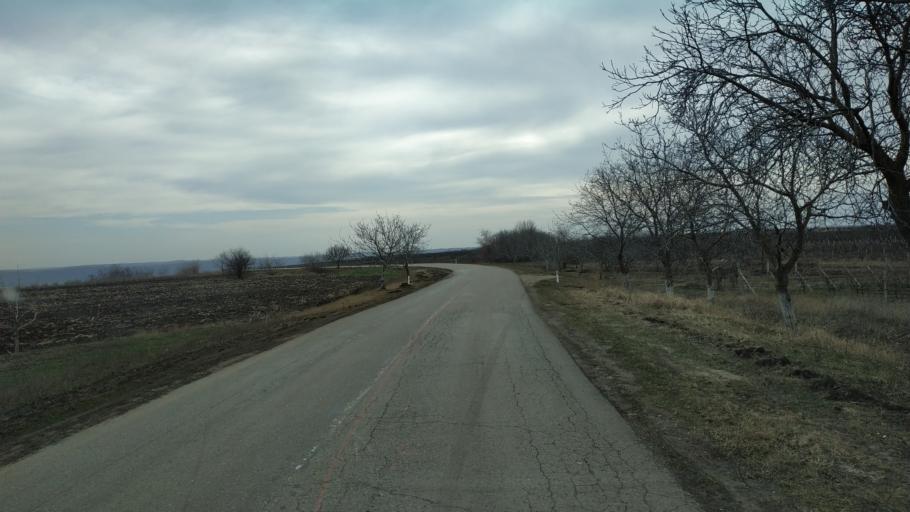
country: MD
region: Nisporeni
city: Nisporeni
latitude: 46.9452
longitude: 28.2421
